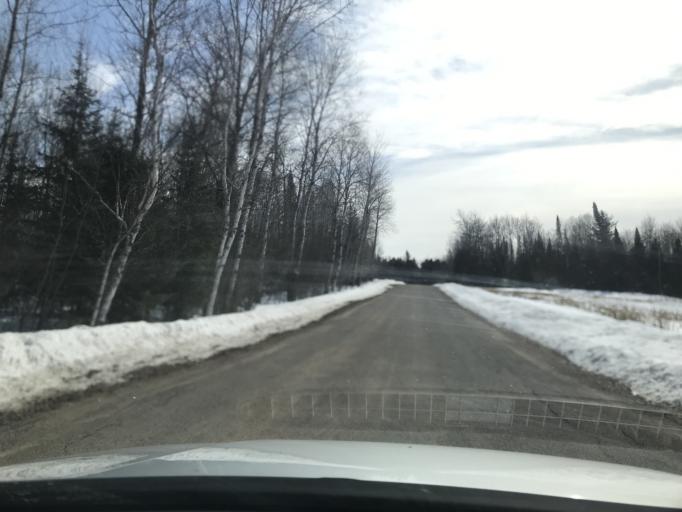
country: US
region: Wisconsin
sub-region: Marinette County
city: Peshtigo
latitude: 45.2947
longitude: -87.8389
